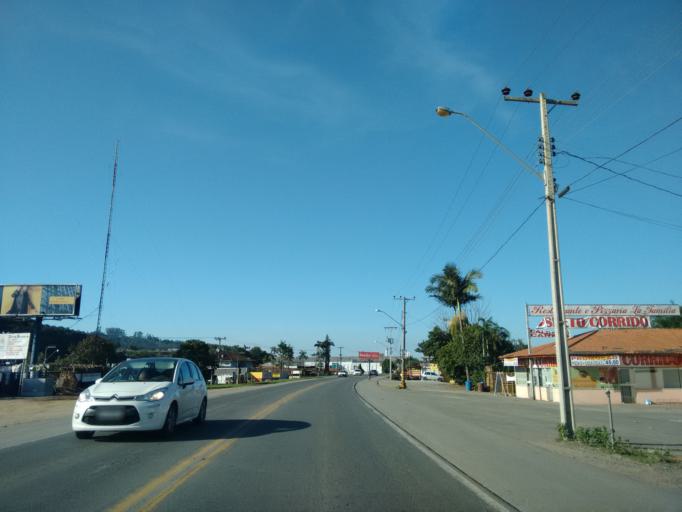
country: BR
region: Santa Catarina
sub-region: Guaramirim
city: Guaramirim
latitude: -26.4760
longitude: -48.9939
